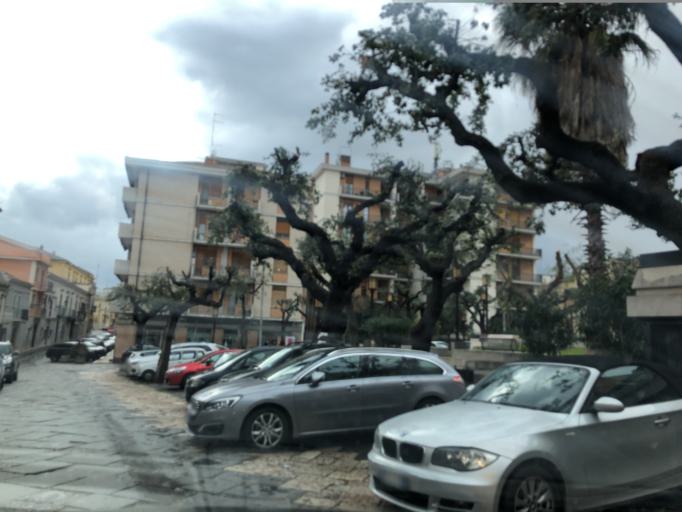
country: IT
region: Apulia
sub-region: Provincia di Foggia
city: Lucera
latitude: 41.5105
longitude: 15.3342
